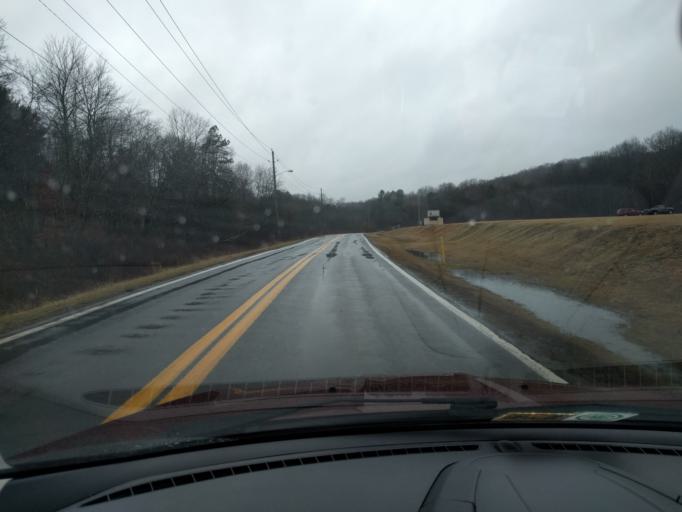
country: US
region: West Virginia
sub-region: Raleigh County
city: Beckley
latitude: 37.7926
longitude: -81.1930
